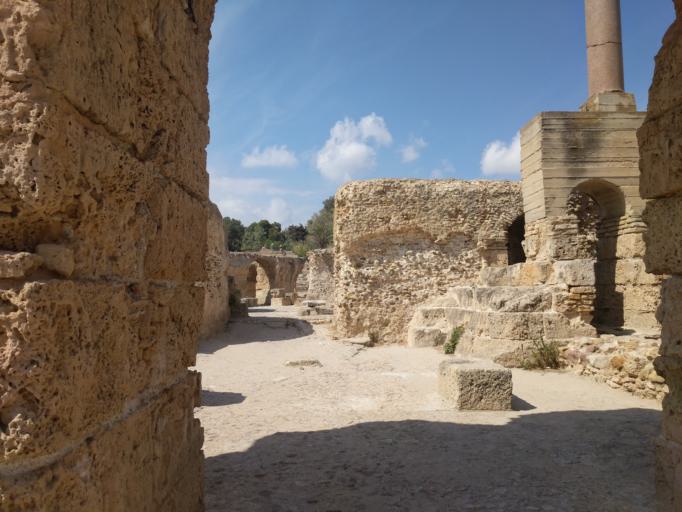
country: TN
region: Tunis
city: Carthage
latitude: 36.8545
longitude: 10.3353
